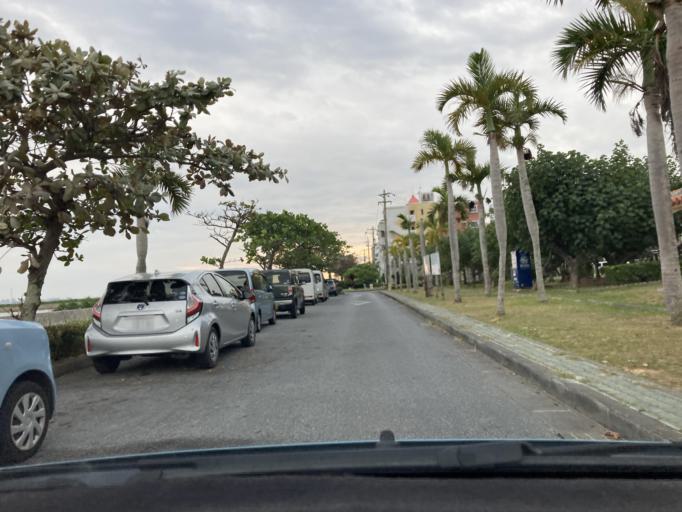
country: JP
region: Okinawa
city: Chatan
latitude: 26.3218
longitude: 127.7520
